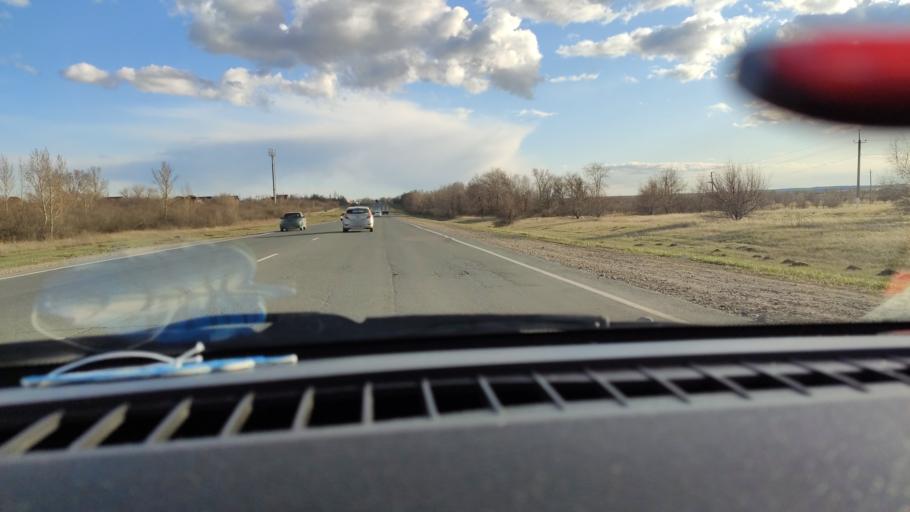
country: RU
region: Saratov
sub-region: Saratovskiy Rayon
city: Saratov
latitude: 51.6846
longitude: 46.0025
